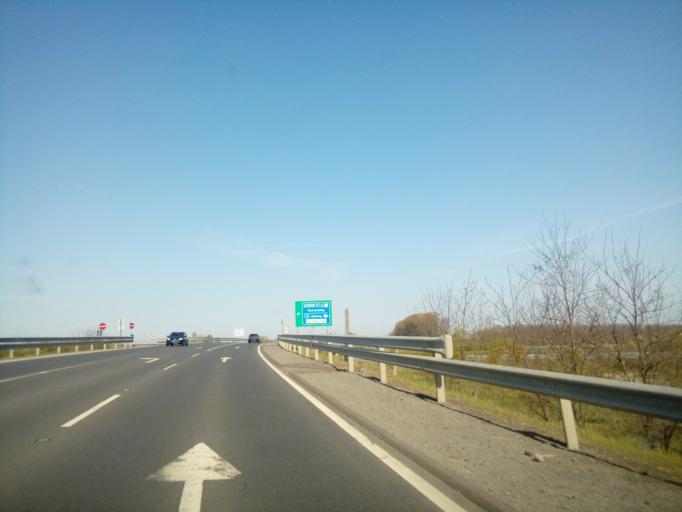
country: HU
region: Szabolcs-Szatmar-Bereg
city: Nagykallo
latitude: 47.8917
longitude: 21.8063
